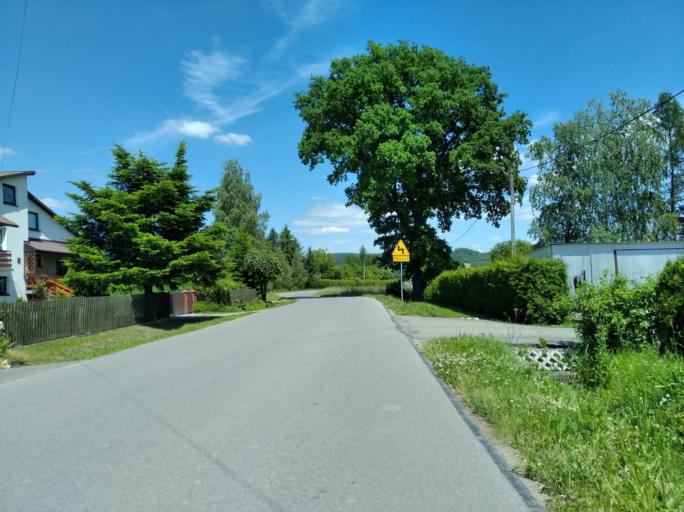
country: PL
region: Subcarpathian Voivodeship
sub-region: Powiat krosnienski
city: Wojaszowka
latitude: 49.7806
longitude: 21.6738
